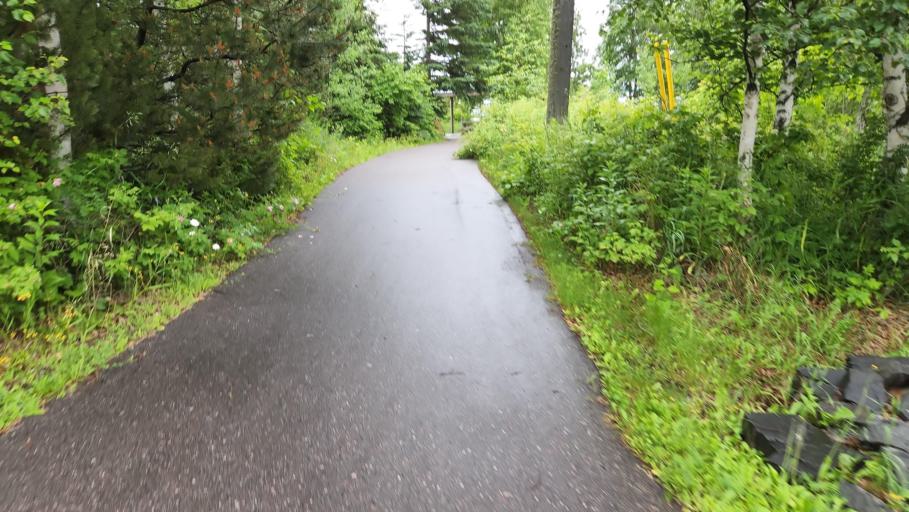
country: CA
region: Ontario
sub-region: Thunder Bay District
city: Thunder Bay
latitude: 48.4531
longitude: -89.1839
